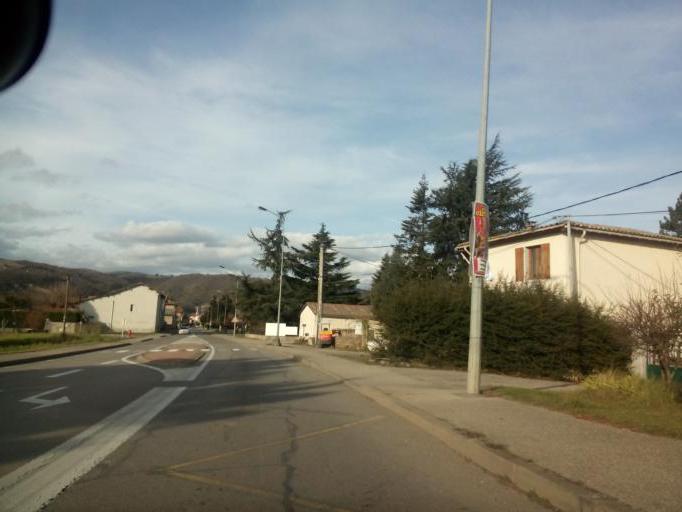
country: FR
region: Rhone-Alpes
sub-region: Departement de l'Isere
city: Sablons
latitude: 45.3174
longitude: 4.7835
